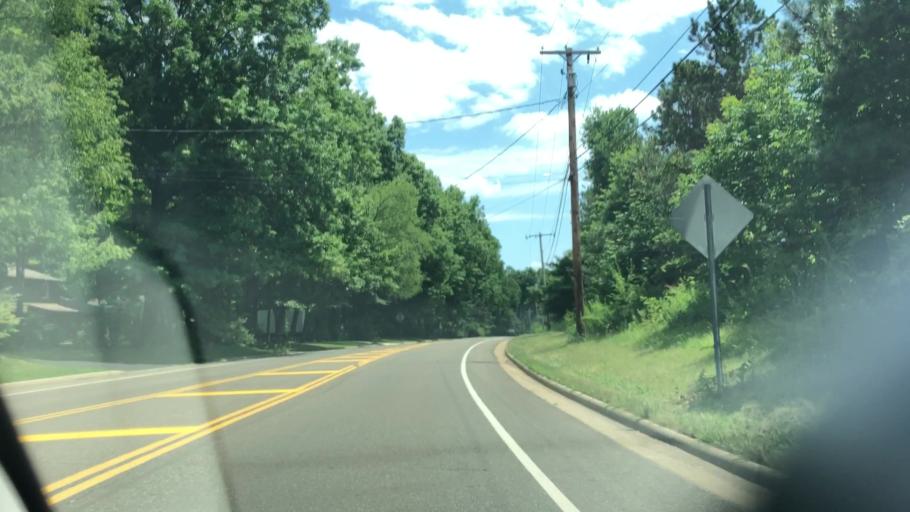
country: US
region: Ohio
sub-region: Summit County
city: Greensburg
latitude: 40.8717
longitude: -81.4993
